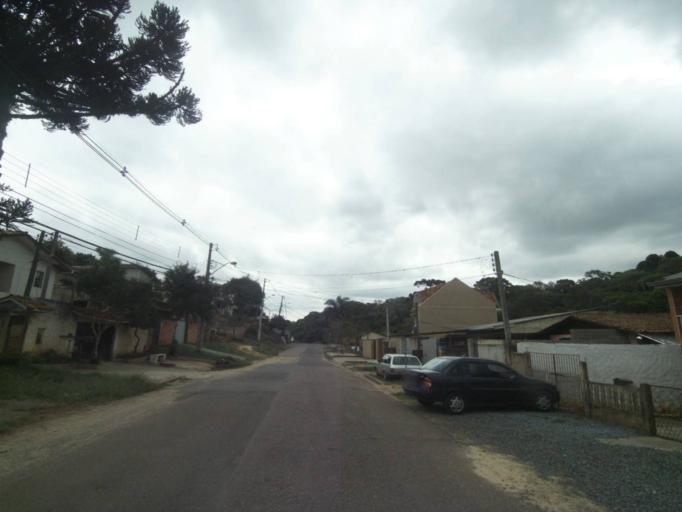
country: BR
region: Parana
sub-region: Curitiba
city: Curitiba
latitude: -25.3868
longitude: -49.2936
